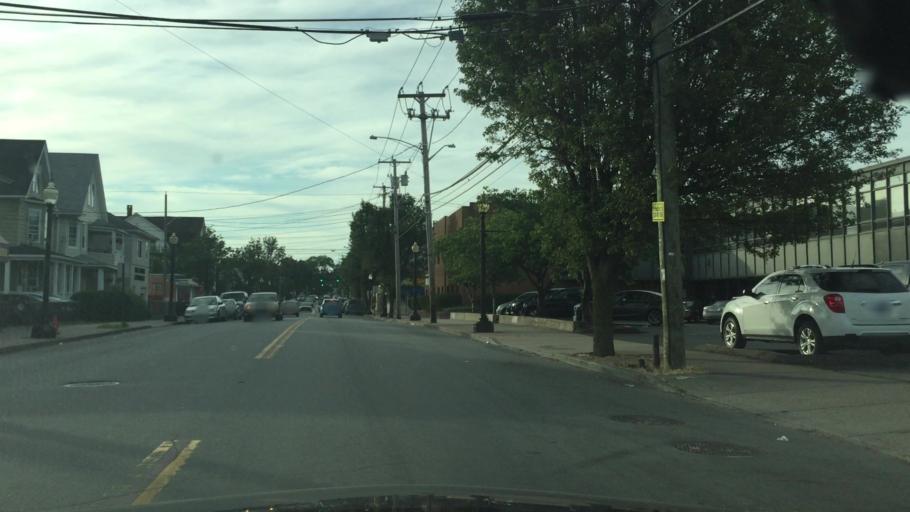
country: US
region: Connecticut
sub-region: Fairfield County
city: Bridgeport
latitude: 41.1928
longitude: -73.2048
